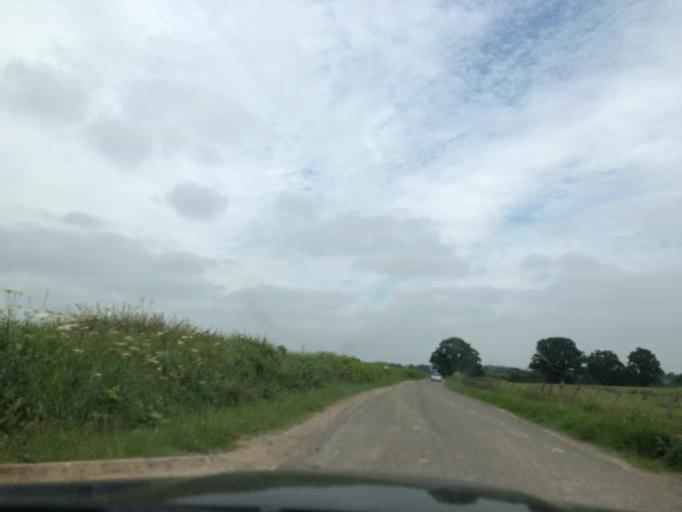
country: GB
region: England
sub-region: Warwickshire
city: Kenilworth
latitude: 52.3346
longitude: -1.6232
